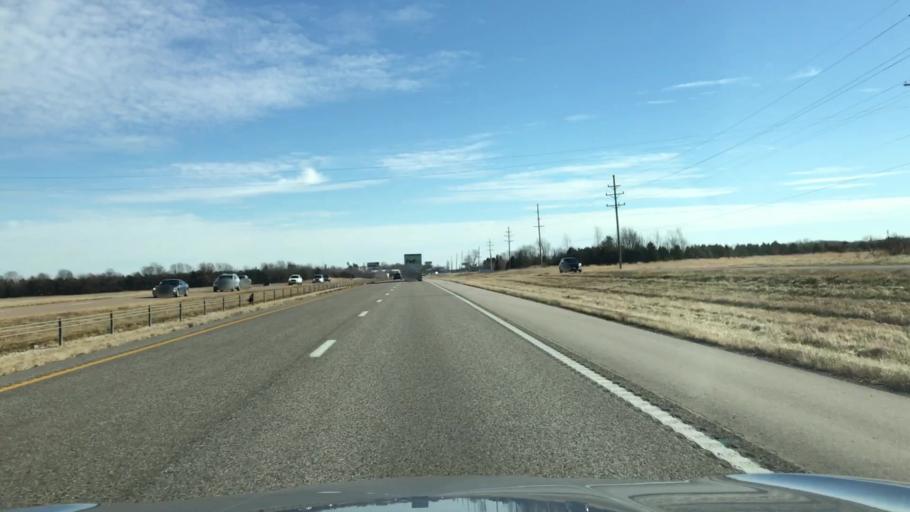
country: US
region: Missouri
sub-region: Montgomery County
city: Montgomery City
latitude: 38.8848
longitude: -91.4003
